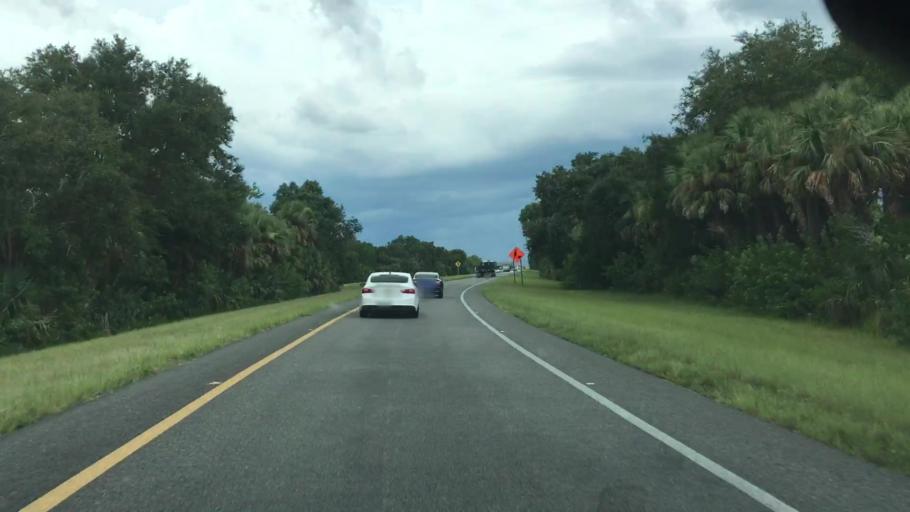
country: US
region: Florida
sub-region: Brevard County
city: Port Saint John
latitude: 28.4531
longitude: -80.8745
